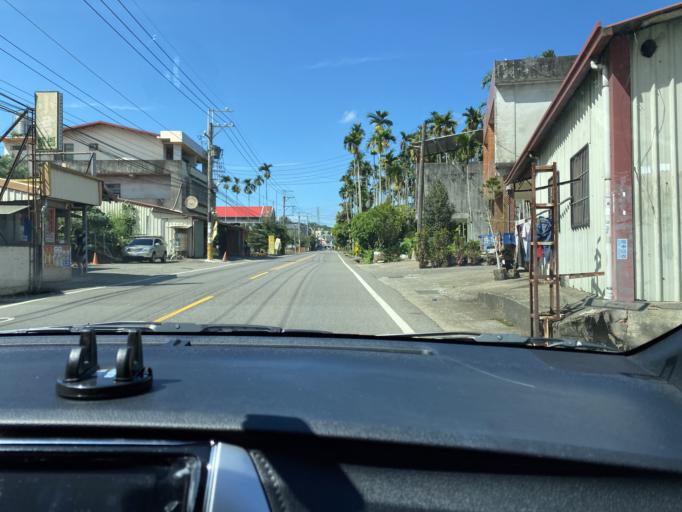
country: TW
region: Taiwan
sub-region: Nantou
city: Nantou
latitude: 23.8597
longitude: 120.6315
